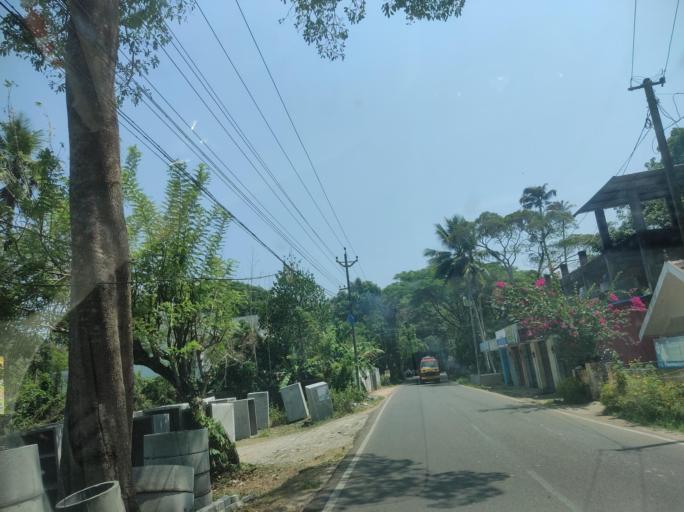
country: IN
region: Kerala
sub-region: Alappuzha
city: Kutiatodu
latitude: 9.8331
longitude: 76.2977
